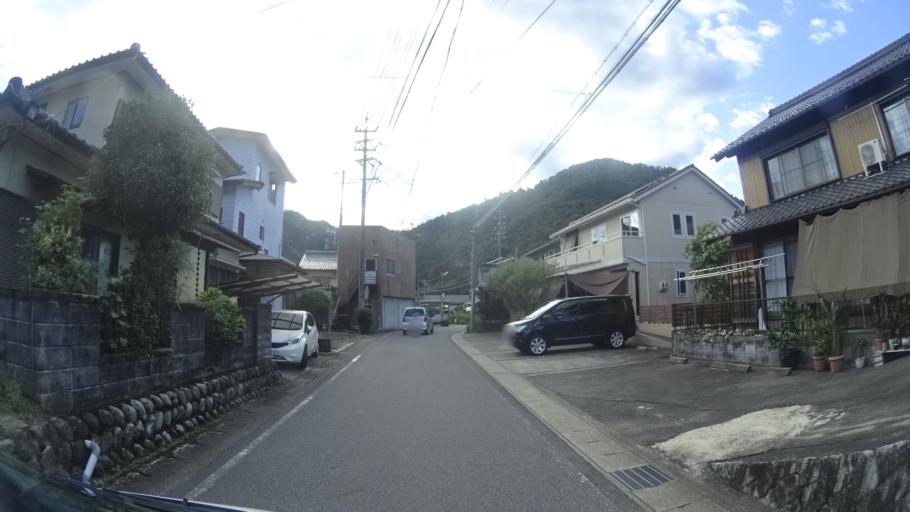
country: JP
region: Gifu
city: Minokamo
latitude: 35.5419
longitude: 137.1218
